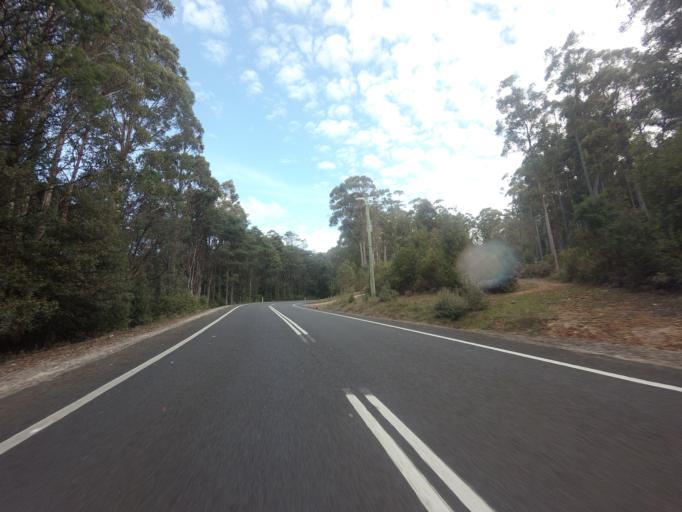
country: AU
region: Tasmania
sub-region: Meander Valley
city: Deloraine
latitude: -41.6410
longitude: 146.7185
